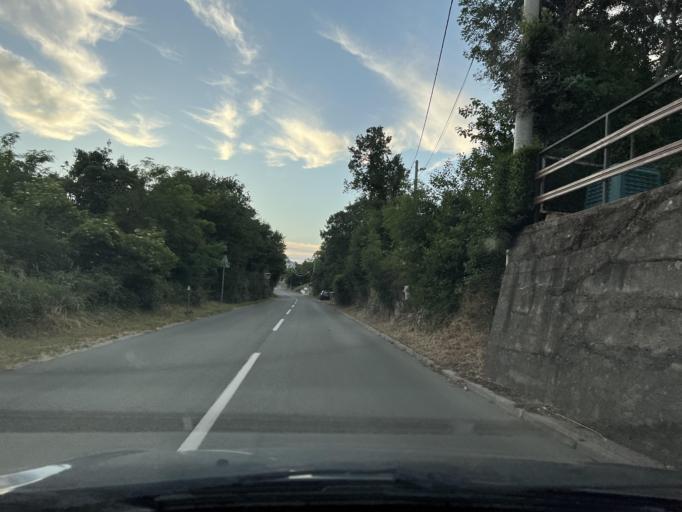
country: HR
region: Primorsko-Goranska
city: Marcelji
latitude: 45.3971
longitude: 14.3975
